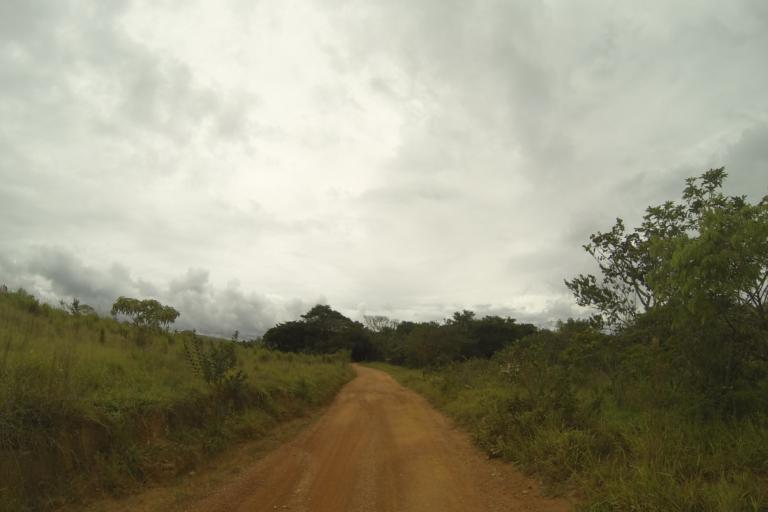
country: BR
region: Minas Gerais
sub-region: Ibia
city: Ibia
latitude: -19.7465
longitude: -46.5343
